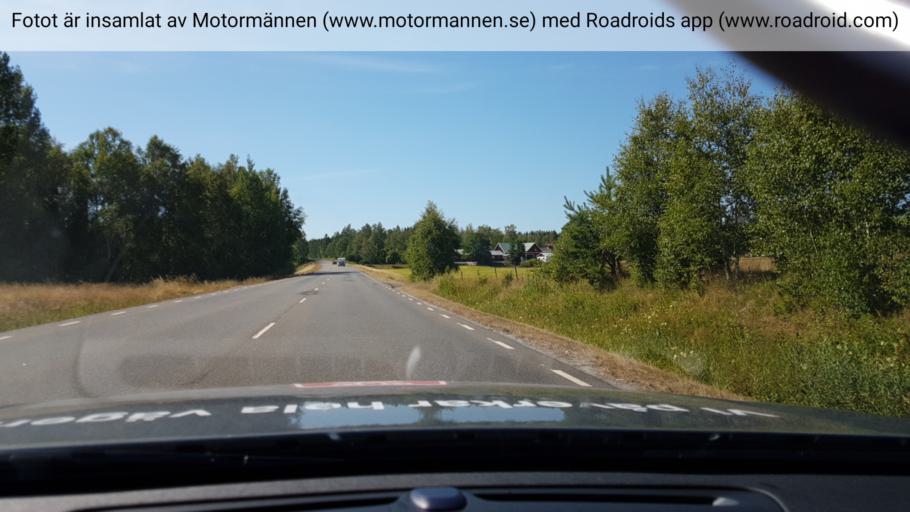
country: SE
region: Vaestra Goetaland
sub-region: Karlsborgs Kommun
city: Karlsborg
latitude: 58.5742
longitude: 14.4767
